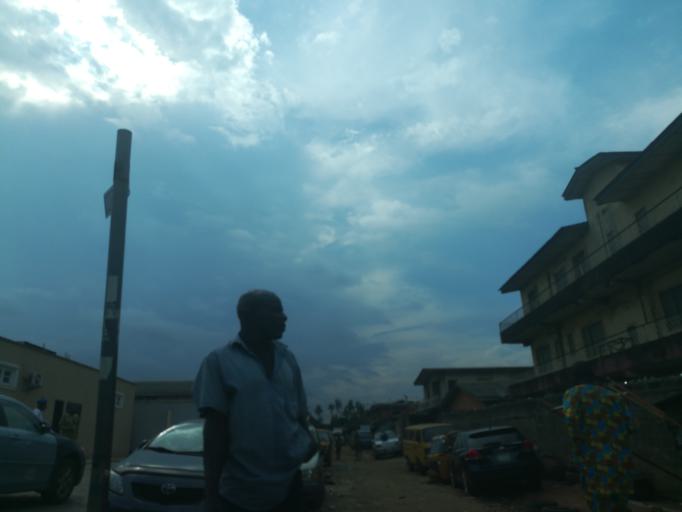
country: NG
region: Lagos
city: Ikorodu
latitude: 6.6232
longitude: 3.5027
